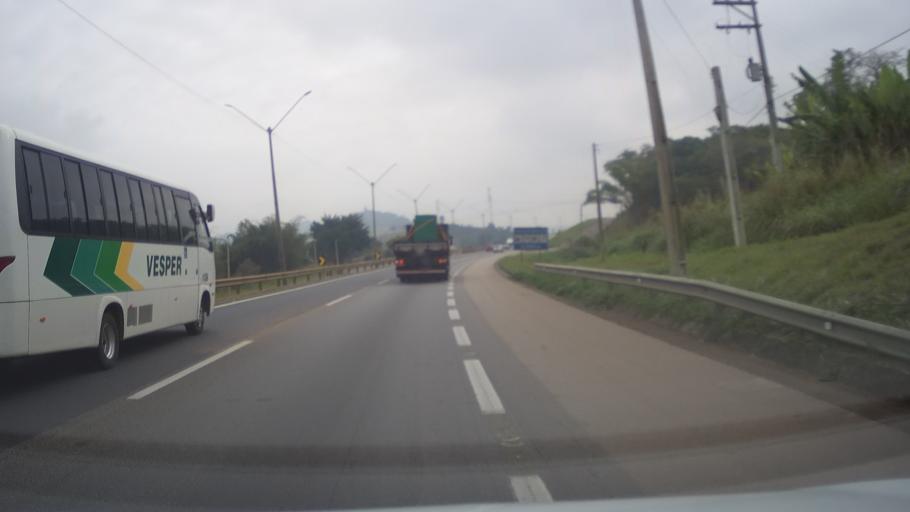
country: BR
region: Sao Paulo
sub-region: Atibaia
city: Atibaia
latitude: -23.0384
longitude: -46.5557
